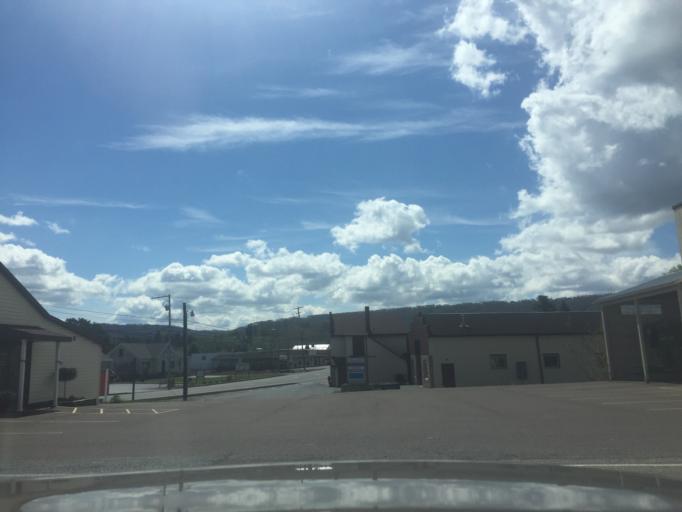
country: US
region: Pennsylvania
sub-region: Luzerne County
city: Conyngham
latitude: 41.0022
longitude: -76.0749
